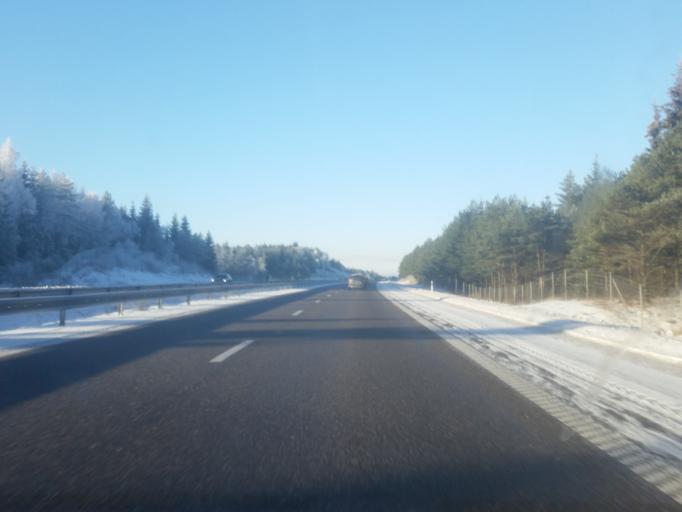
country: SE
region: Vaestra Goetaland
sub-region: Harryda Kommun
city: Hindas
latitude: 57.6683
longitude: 12.3872
